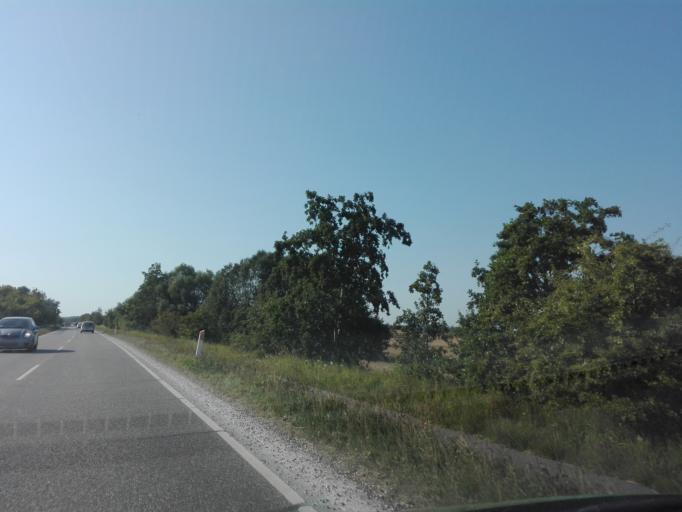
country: DK
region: Central Jutland
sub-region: Odder Kommune
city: Odder
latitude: 55.9591
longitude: 10.1853
